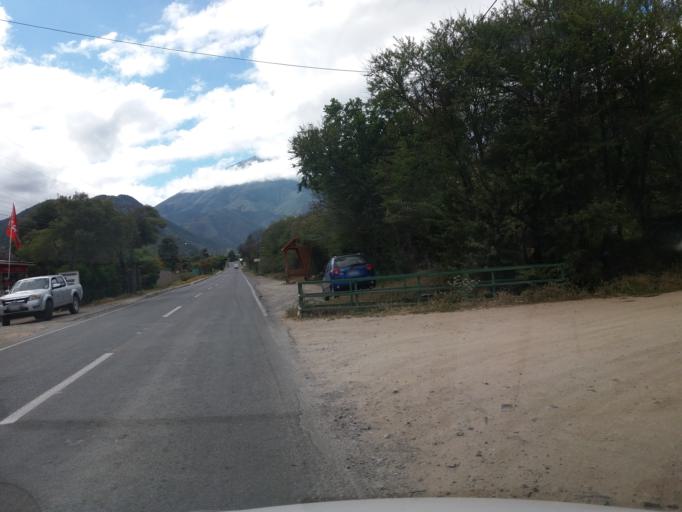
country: CL
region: Valparaiso
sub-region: Provincia de Marga Marga
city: Limache
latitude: -33.0514
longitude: -71.0995
